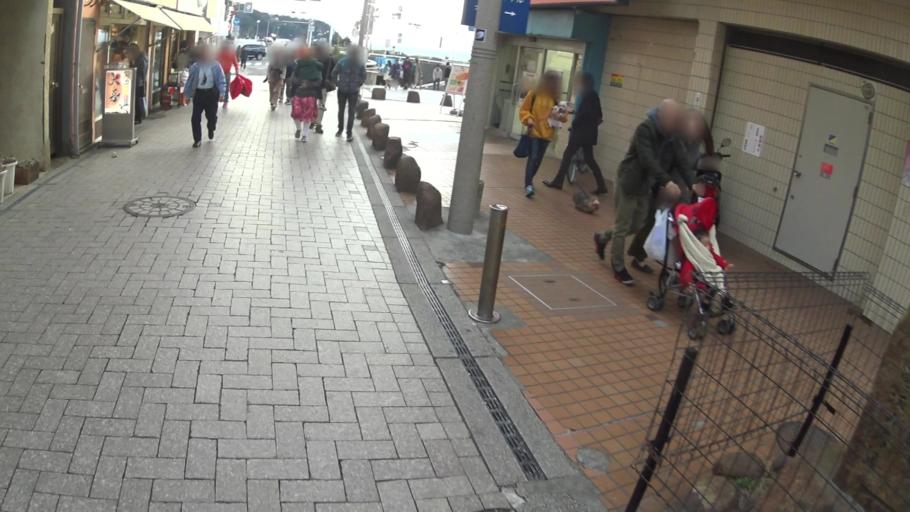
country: JP
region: Kanagawa
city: Fujisawa
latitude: 35.3086
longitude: 139.4857
